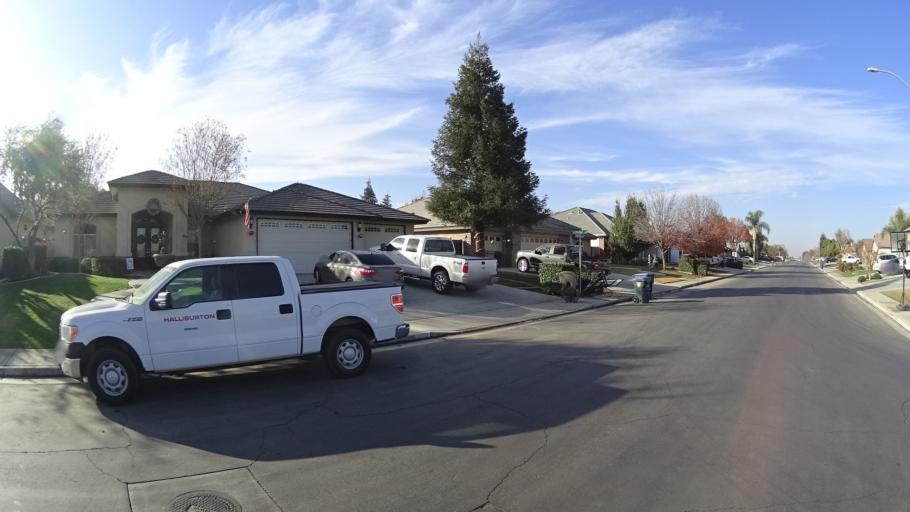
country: US
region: California
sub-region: Kern County
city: Rosedale
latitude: 35.4093
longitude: -119.1337
